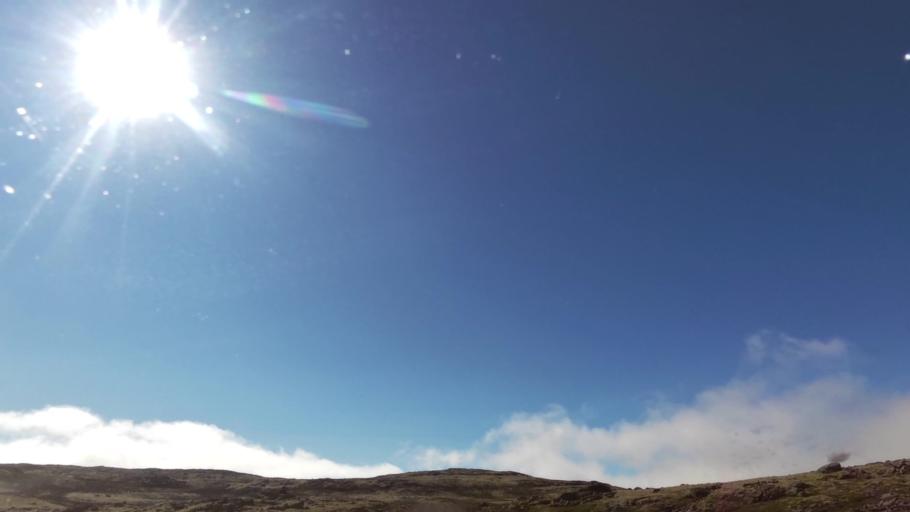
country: IS
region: West
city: Olafsvik
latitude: 65.5512
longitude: -24.2122
